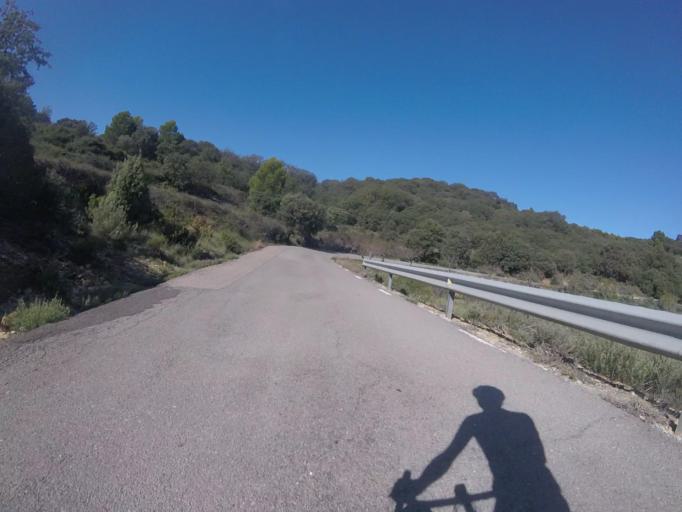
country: ES
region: Valencia
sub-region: Provincia de Castello
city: Sarratella
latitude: 40.3048
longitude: 0.0308
